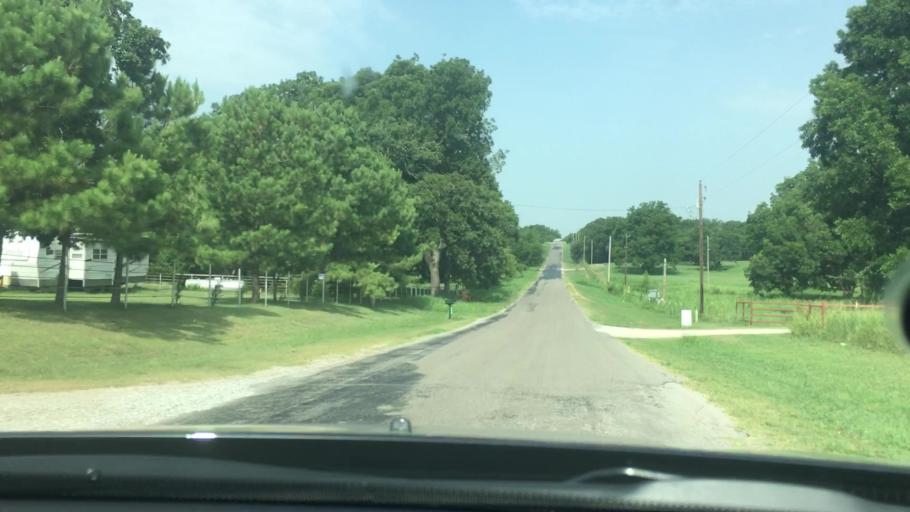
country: US
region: Oklahoma
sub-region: Garvin County
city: Pauls Valley
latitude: 34.8259
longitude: -97.2051
